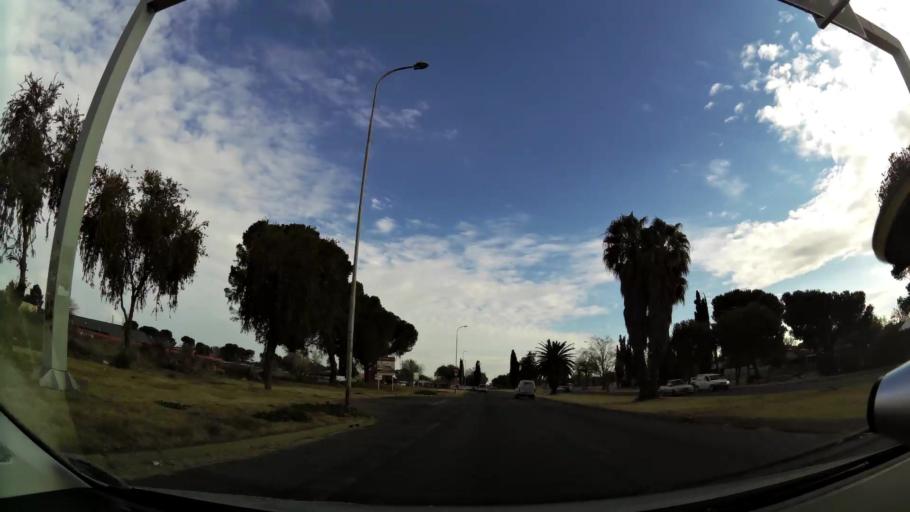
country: ZA
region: Orange Free State
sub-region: Lejweleputswa District Municipality
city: Welkom
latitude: -27.9861
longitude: 26.7573
